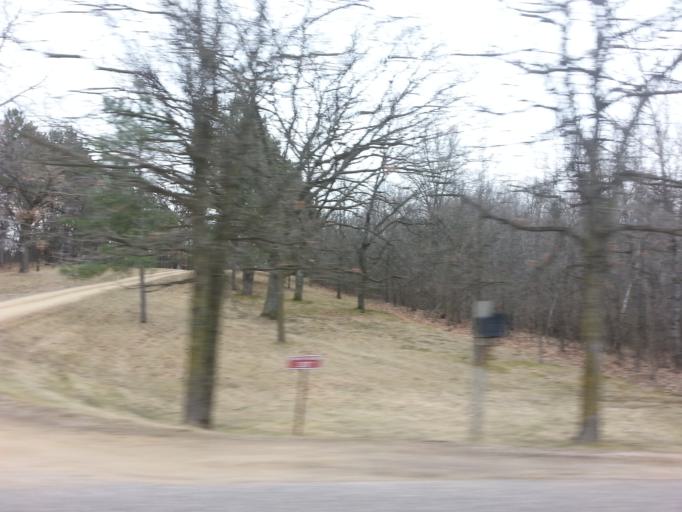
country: US
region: Wisconsin
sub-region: Saint Croix County
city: North Hudson
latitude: 45.0081
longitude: -92.7399
